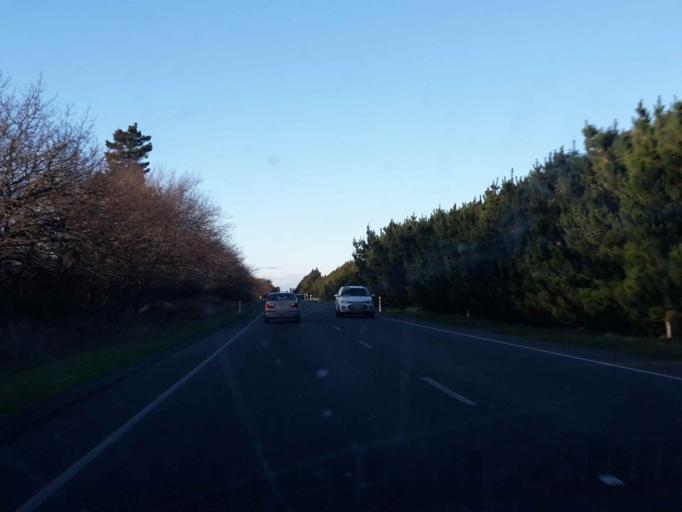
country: NZ
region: Canterbury
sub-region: Selwyn District
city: Burnham
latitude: -43.6226
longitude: 172.2953
